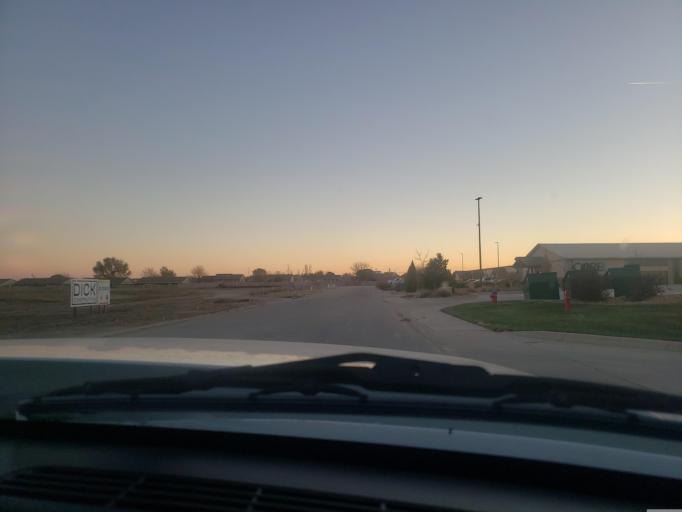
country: US
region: Kansas
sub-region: Finney County
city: Garden City
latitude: 37.9730
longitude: -100.8365
